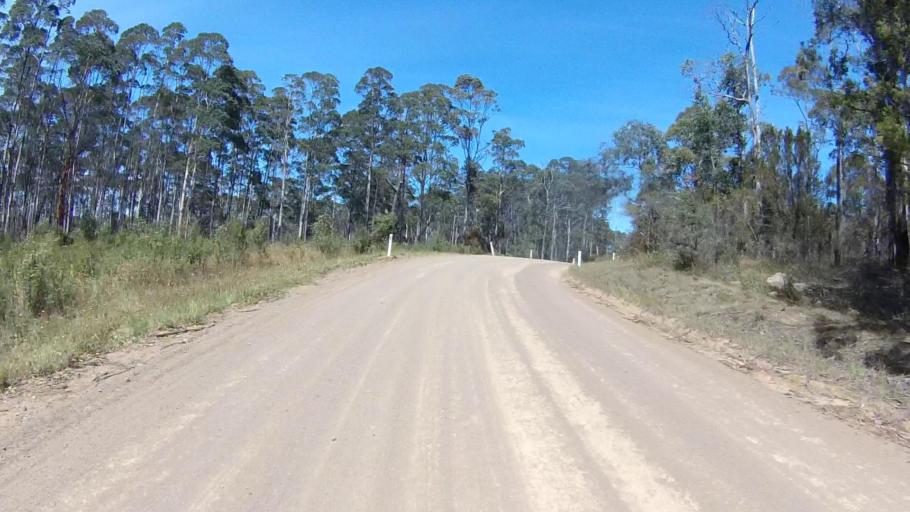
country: AU
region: Tasmania
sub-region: Sorell
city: Sorell
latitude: -42.7276
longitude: 147.7416
